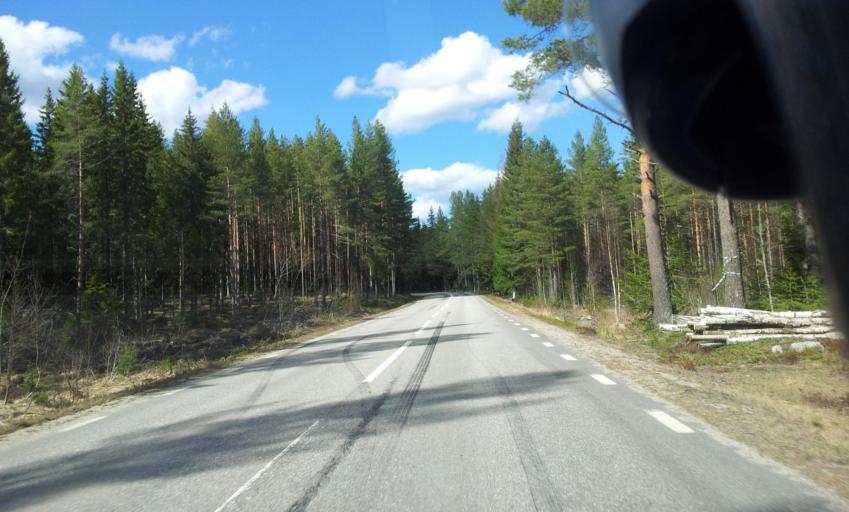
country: SE
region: Gaevleborg
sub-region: Ovanakers Kommun
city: Edsbyn
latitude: 61.3532
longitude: 15.8137
